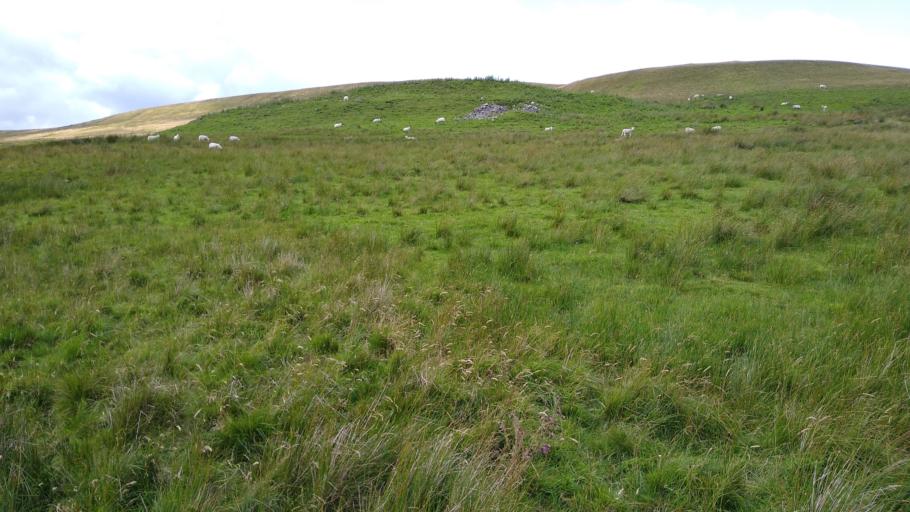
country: GB
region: England
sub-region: County Durham
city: Holwick
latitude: 54.7699
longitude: -2.2744
